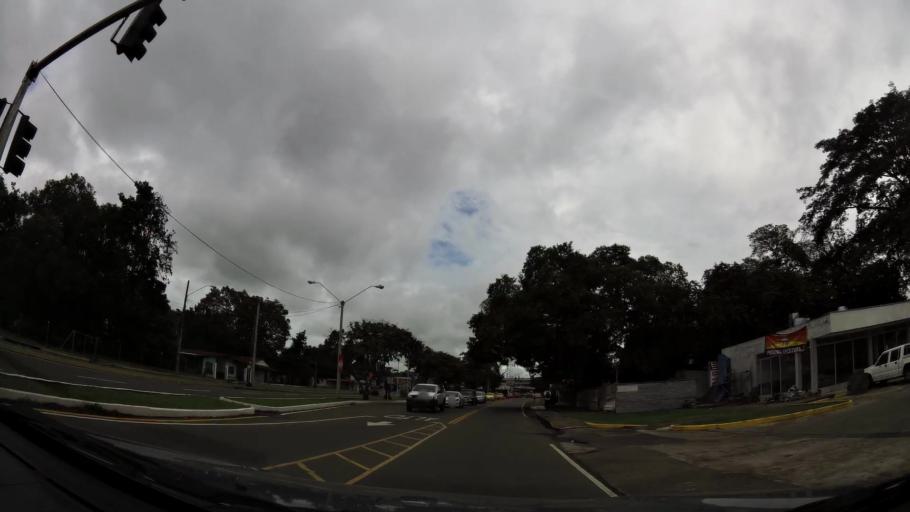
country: PA
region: Chiriqui
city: David
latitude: 8.4375
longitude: -82.4242
